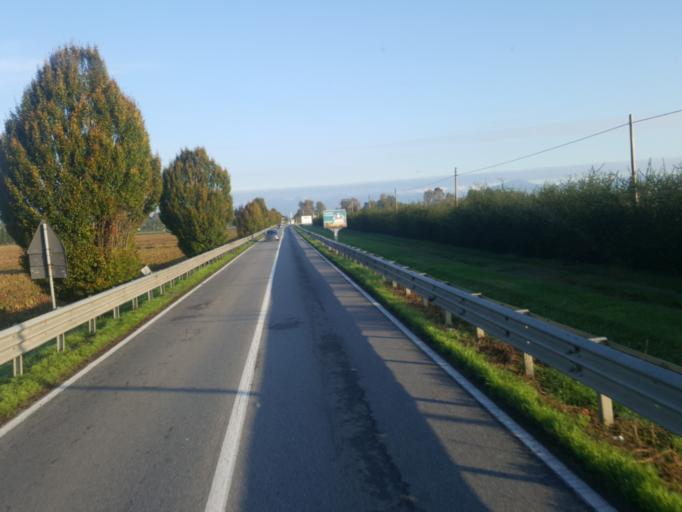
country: IT
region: Lombardy
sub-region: Provincia di Bergamo
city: Morengo
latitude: 45.5481
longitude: 9.7064
